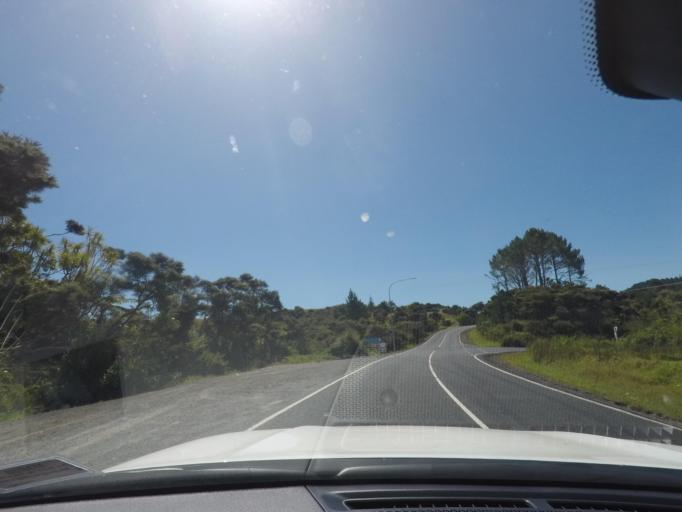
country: NZ
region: Auckland
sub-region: Auckland
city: Parakai
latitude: -36.5846
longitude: 174.3312
